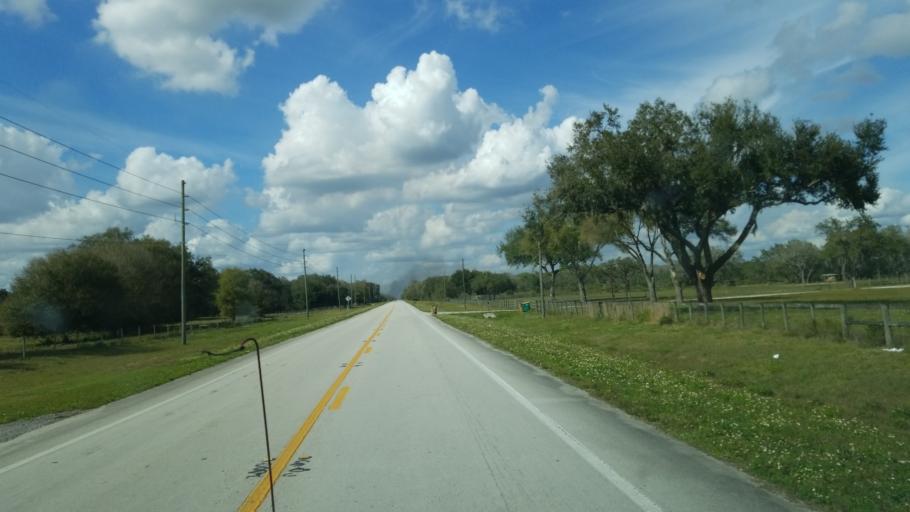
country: US
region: Florida
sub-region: Osceola County
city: Saint Cloud
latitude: 28.0234
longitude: -81.0355
